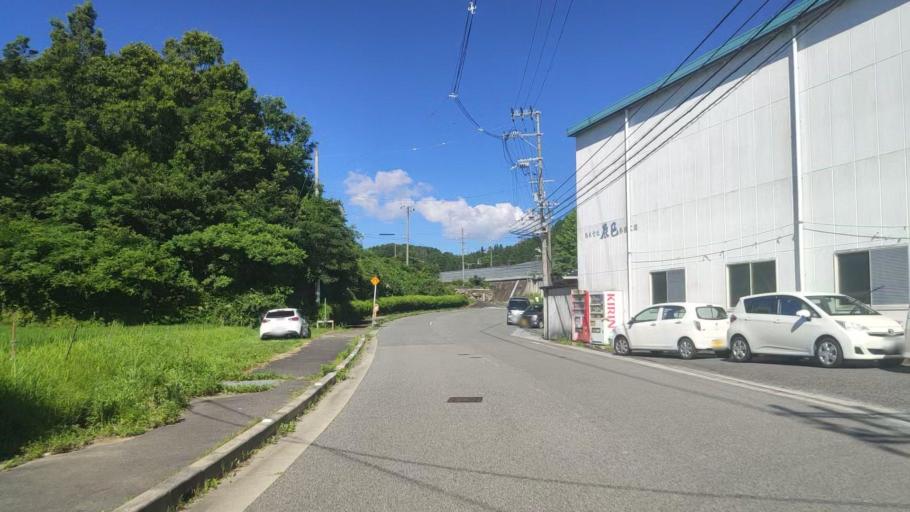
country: JP
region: Nara
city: Haibara-akanedai
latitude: 34.6139
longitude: 135.9632
